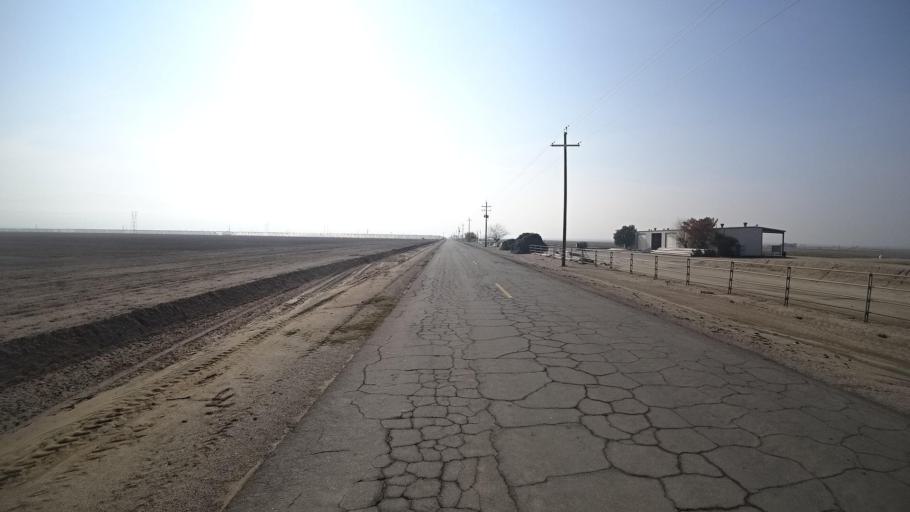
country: US
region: California
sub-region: Kern County
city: Arvin
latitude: 35.0559
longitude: -118.8466
